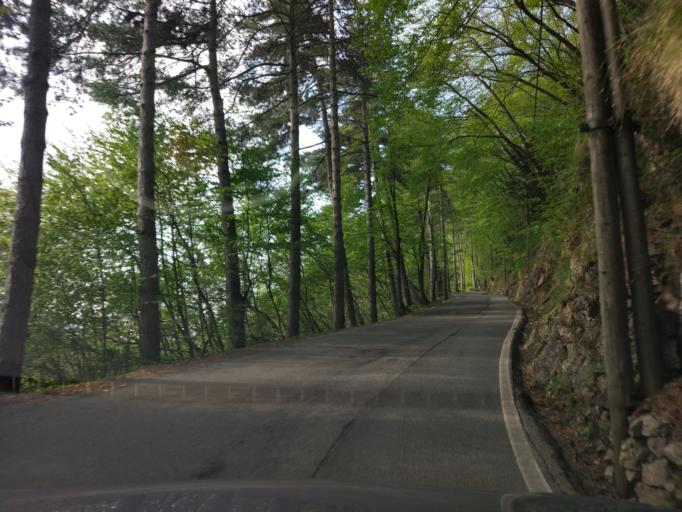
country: IT
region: Lombardy
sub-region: Provincia di Lecco
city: Ballabio
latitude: 45.8997
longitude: 9.4134
